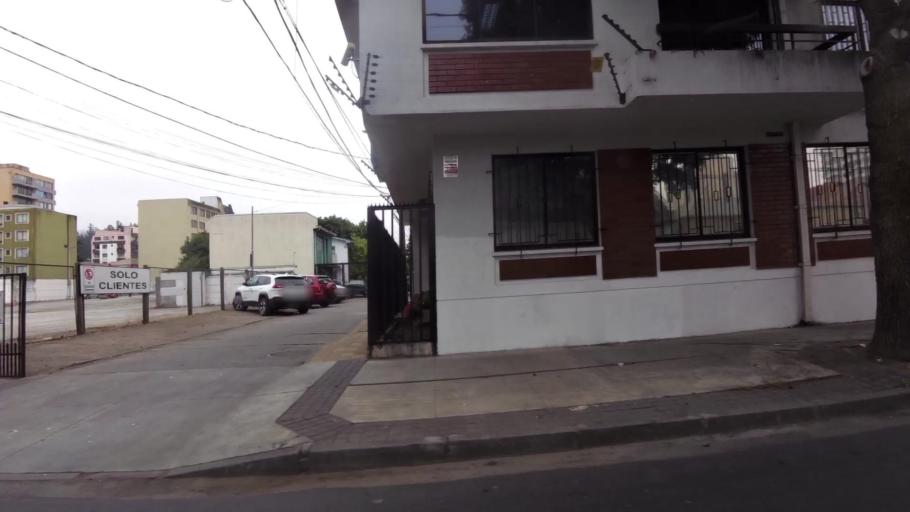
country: CL
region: Biobio
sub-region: Provincia de Concepcion
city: Concepcion
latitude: -36.8209
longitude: -73.0401
